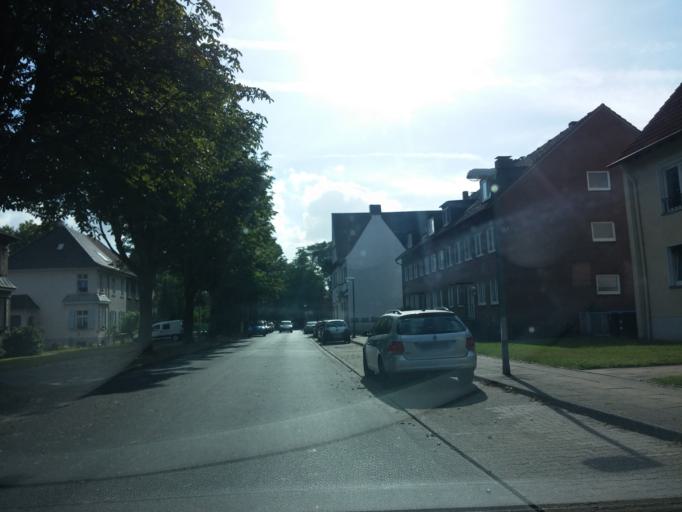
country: DE
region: North Rhine-Westphalia
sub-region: Regierungsbezirk Munster
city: Gladbeck
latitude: 51.5935
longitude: 7.0000
